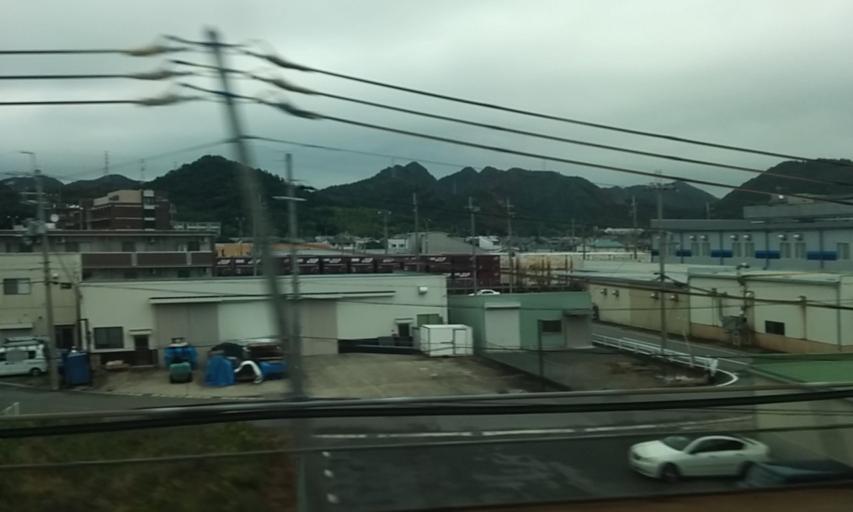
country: JP
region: Hyogo
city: Shirahamacho-usazakiminami
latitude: 34.8046
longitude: 134.7511
